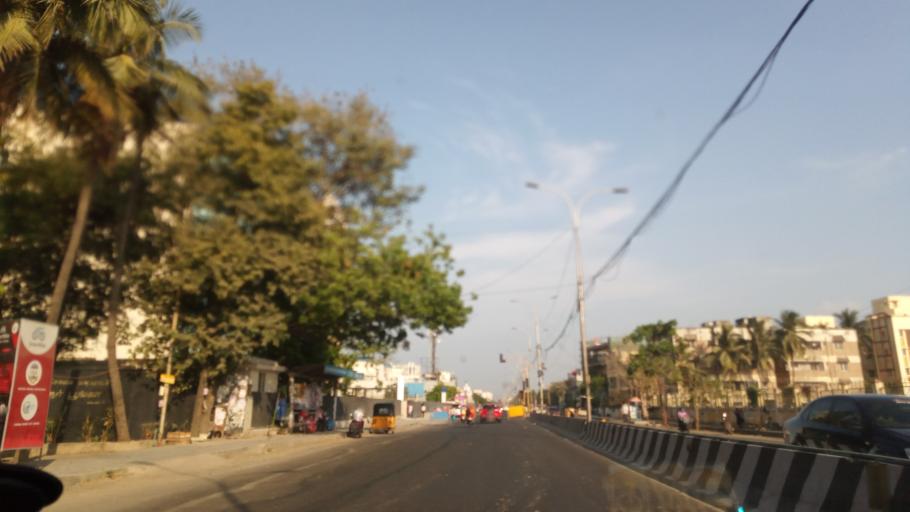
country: IN
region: Tamil Nadu
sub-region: Thiruvallur
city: Porur
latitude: 13.0298
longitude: 80.1681
